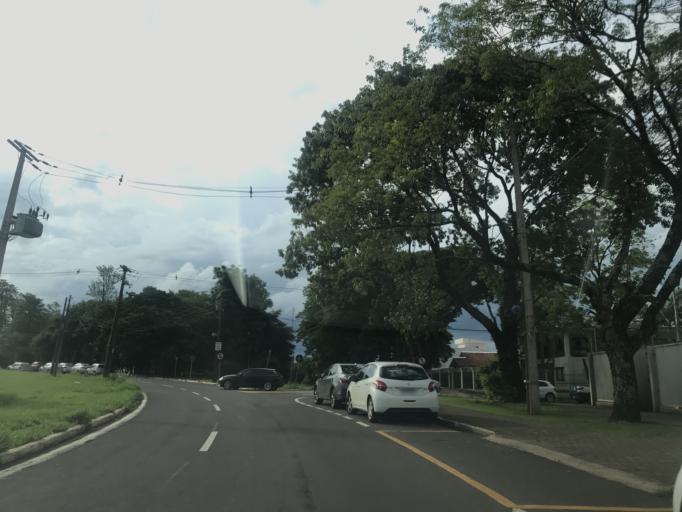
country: BR
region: Parana
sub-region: Maringa
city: Maringa
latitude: -23.4284
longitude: -51.9589
